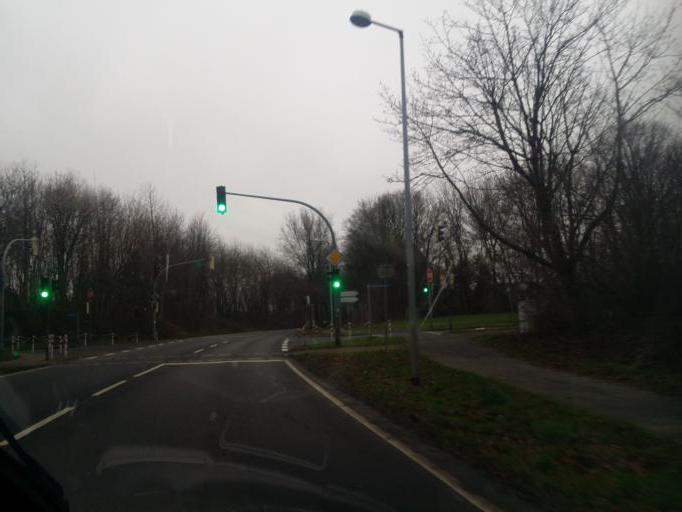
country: DE
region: Schleswig-Holstein
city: Heide
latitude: 54.2022
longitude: 9.1222
